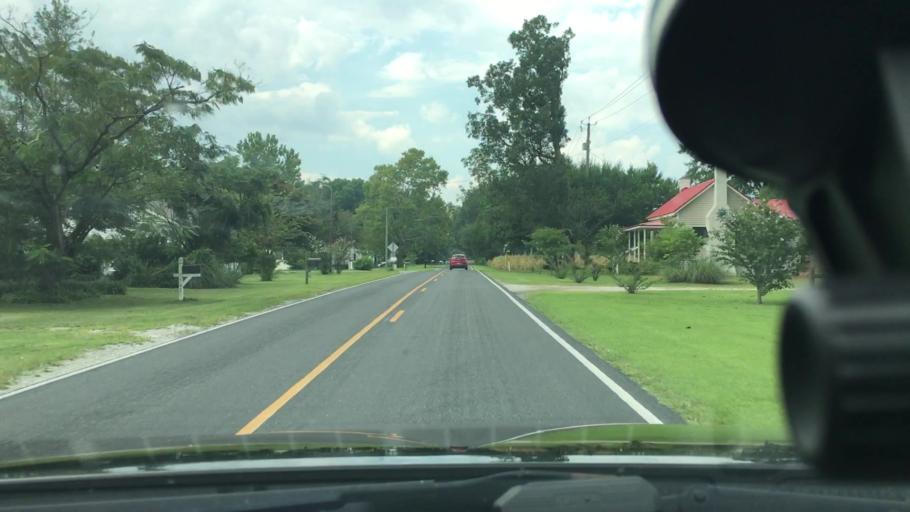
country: US
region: North Carolina
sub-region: Craven County
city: New Bern
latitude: 35.1617
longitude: -77.0471
